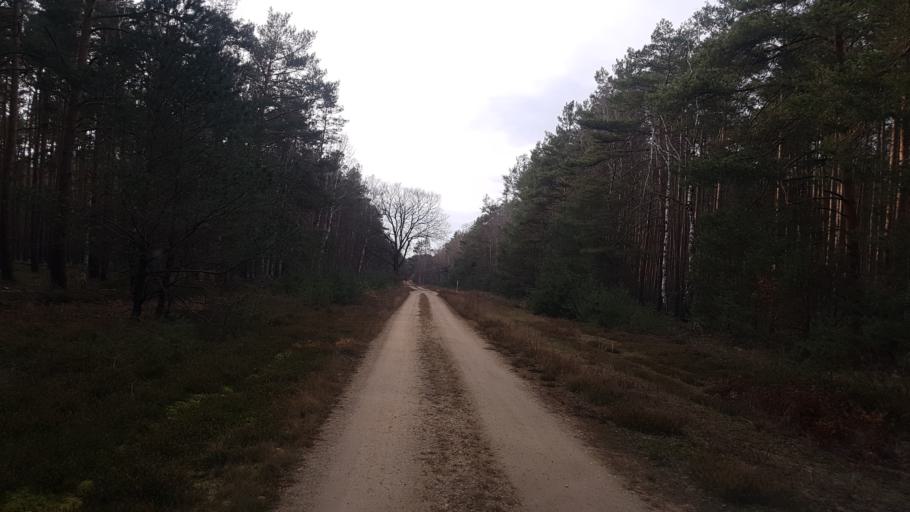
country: DE
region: Brandenburg
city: Trobitz
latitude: 51.5655
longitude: 13.4603
